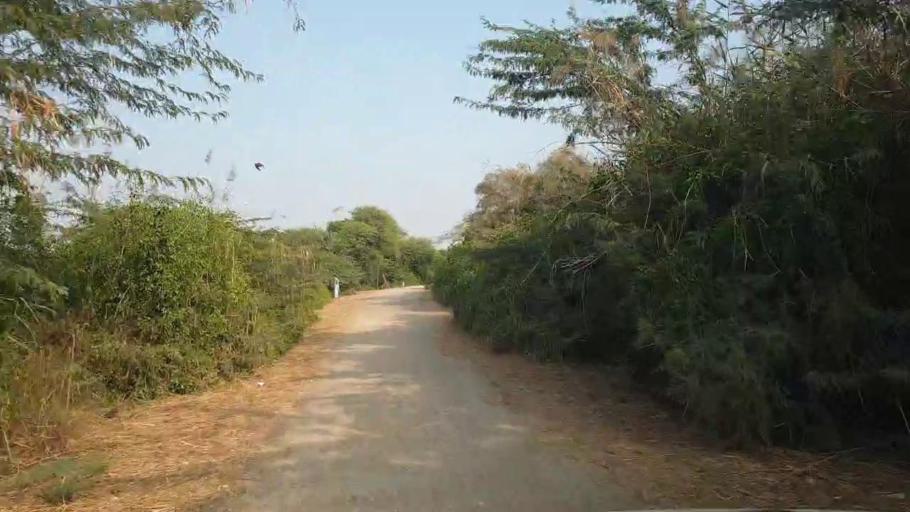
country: PK
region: Sindh
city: Rajo Khanani
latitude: 25.0366
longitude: 68.7719
